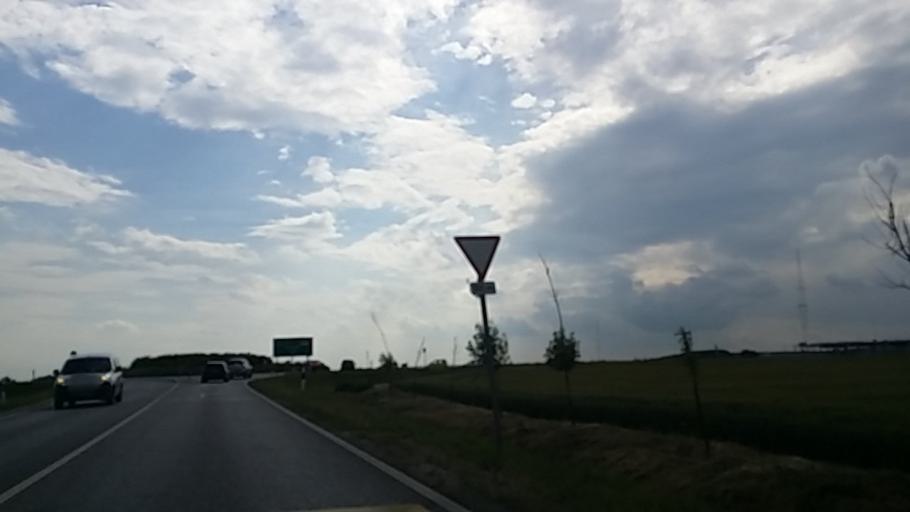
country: HU
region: Pest
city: Szigetszentmiklos
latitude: 47.3715
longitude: 19.0338
